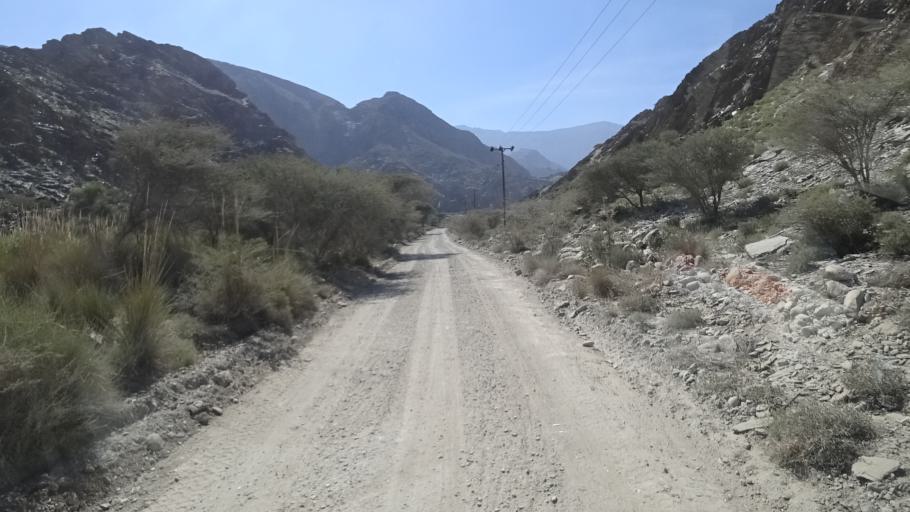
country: OM
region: Al Batinah
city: Bayt al `Awabi
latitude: 23.2309
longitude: 57.4251
